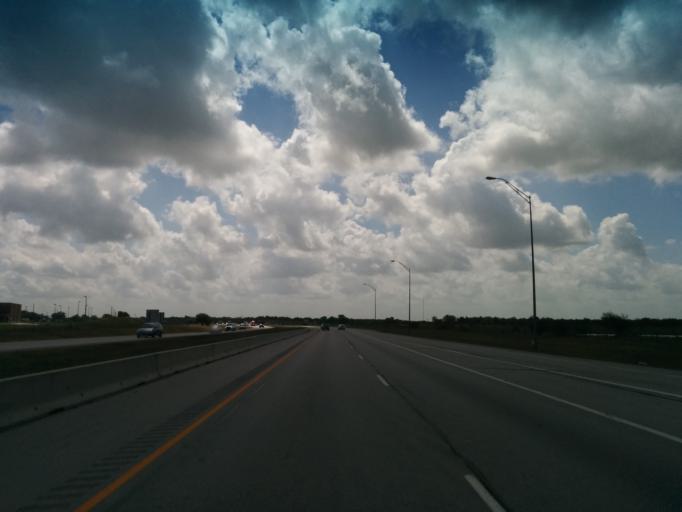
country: US
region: Texas
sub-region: Austin County
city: Sealy
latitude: 29.7610
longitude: -96.1788
